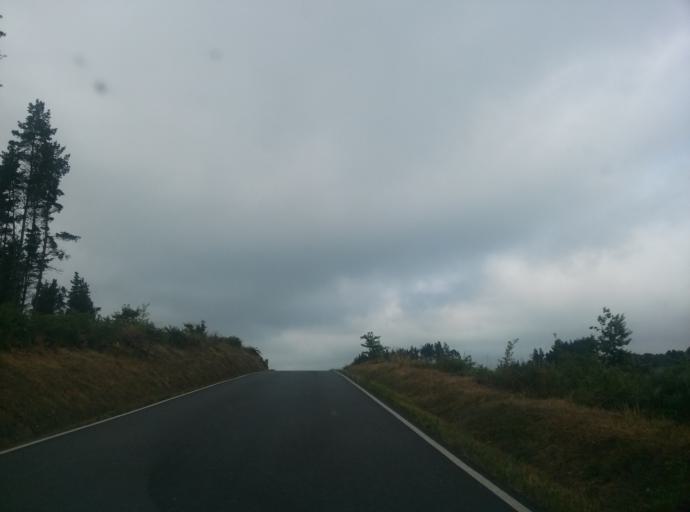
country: ES
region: Galicia
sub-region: Provincia de Lugo
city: Lugo
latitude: 43.0729
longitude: -7.5542
